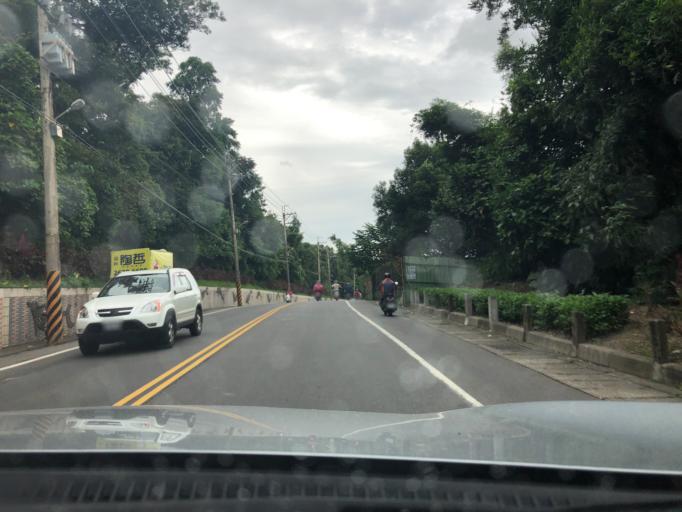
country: TW
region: Taiwan
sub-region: Taoyuan
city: Taoyuan
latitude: 24.9445
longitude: 121.3399
